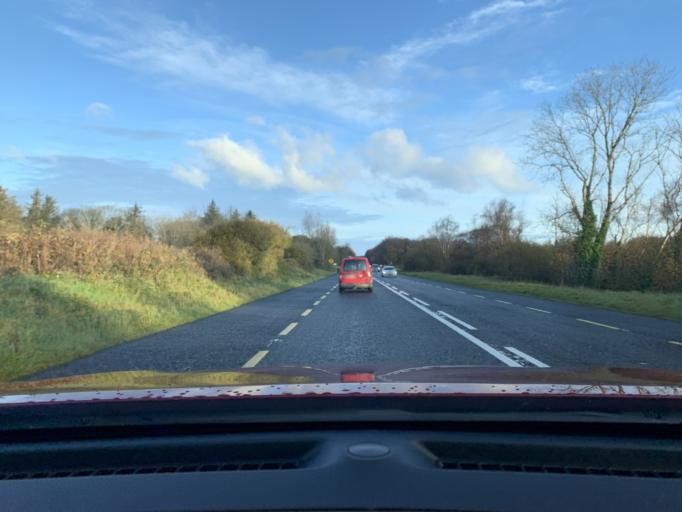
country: IE
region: Connaught
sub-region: Sligo
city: Sligo
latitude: 54.3776
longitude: -8.5289
